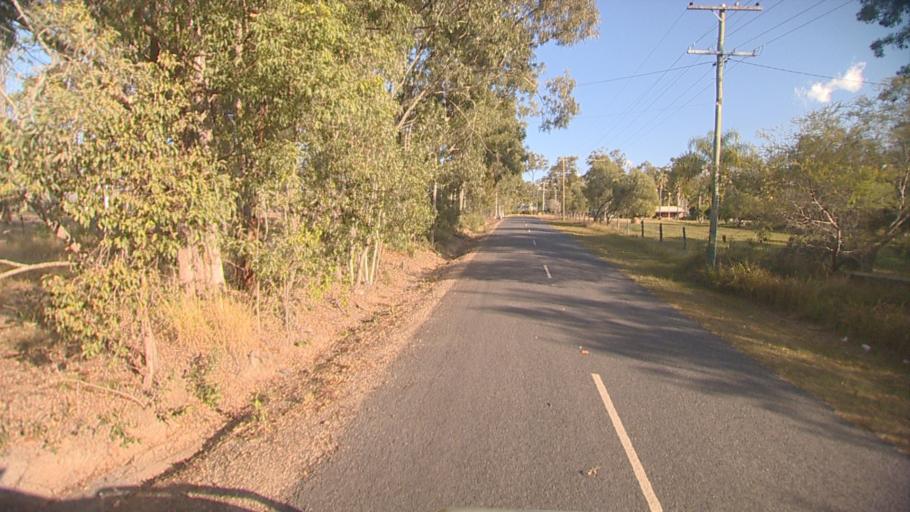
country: AU
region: Queensland
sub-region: Ipswich
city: Springfield Lakes
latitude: -27.6946
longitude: 152.9539
